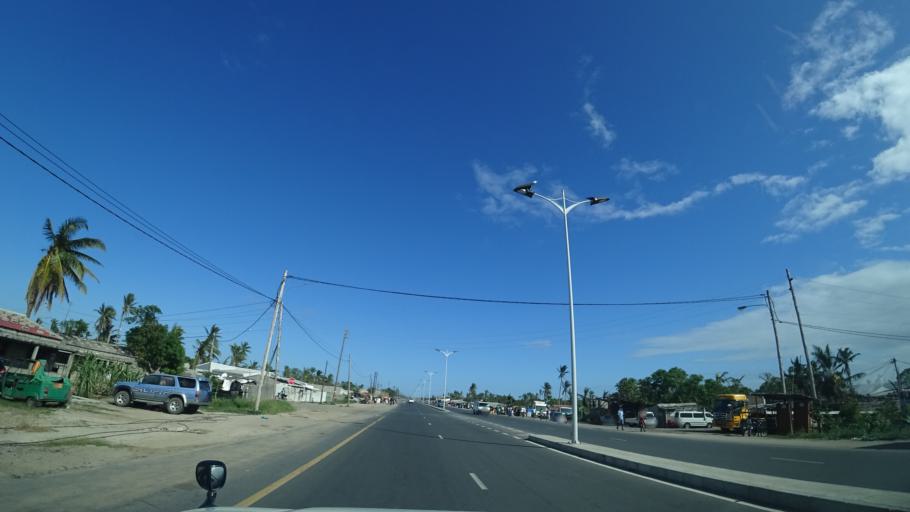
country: MZ
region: Sofala
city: Beira
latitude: -19.7383
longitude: 34.8481
